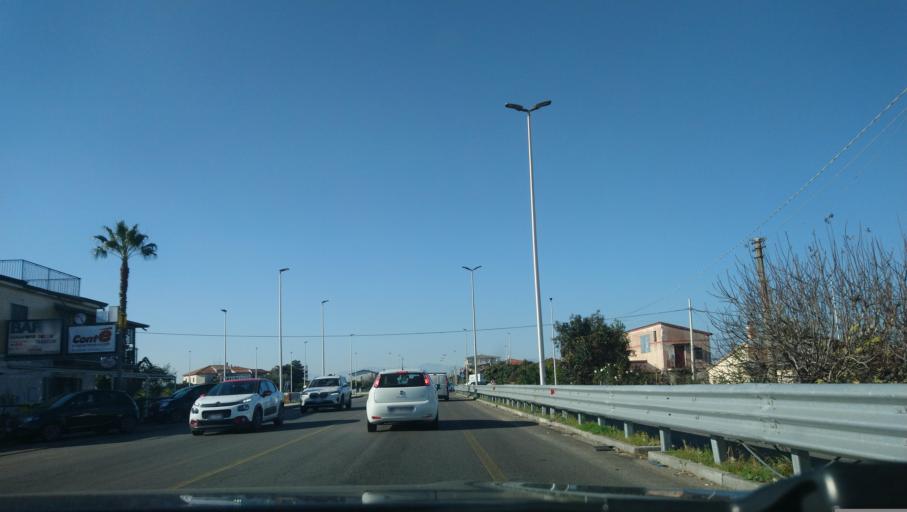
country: IT
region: Calabria
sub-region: Provincia di Cosenza
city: Fabrizio
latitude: 39.6318
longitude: 16.5660
